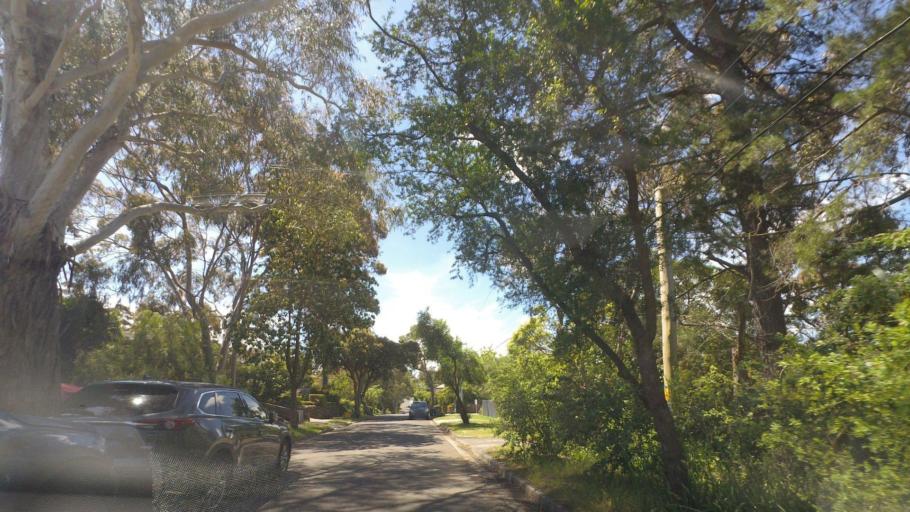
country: AU
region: Victoria
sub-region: Whitehorse
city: Vermont
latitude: -37.8443
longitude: 145.2040
